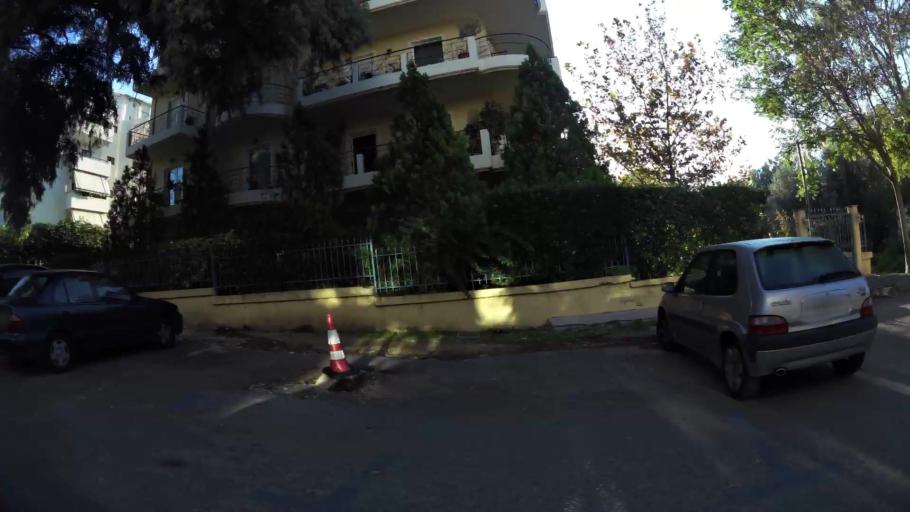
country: GR
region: Attica
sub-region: Nomarchia Athinas
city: Marousi
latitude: 38.0492
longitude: 23.7980
